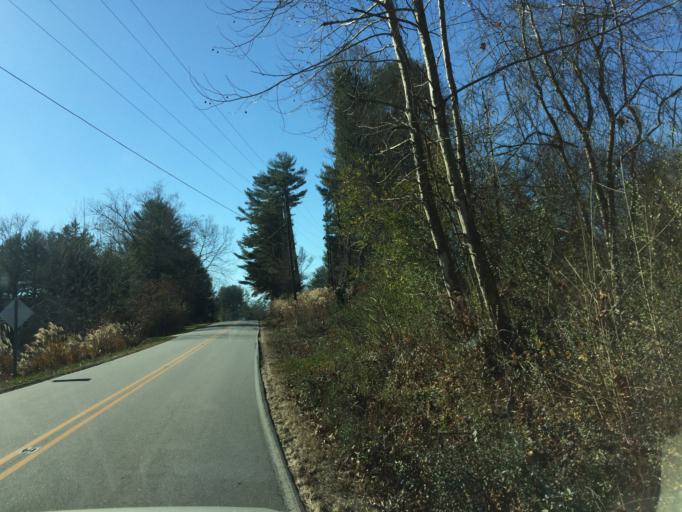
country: US
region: North Carolina
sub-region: Henderson County
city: Mountain Home
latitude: 35.3663
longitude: -82.5249
